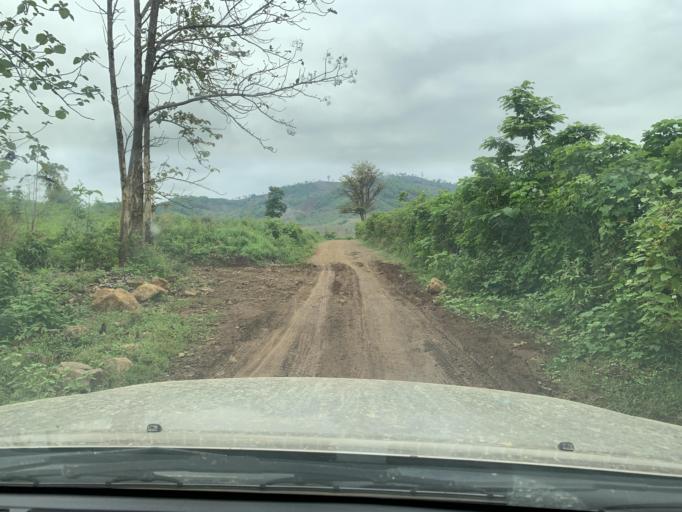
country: TH
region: Uttaradit
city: Ban Khok
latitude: 18.3980
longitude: 101.4301
